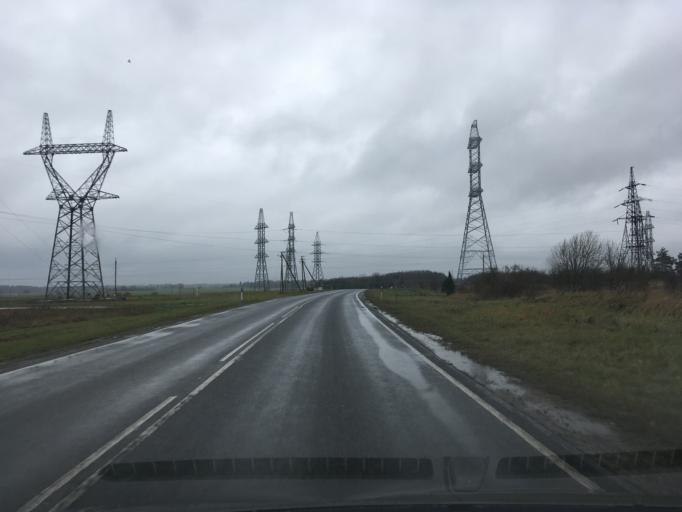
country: EE
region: Laeaene
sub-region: Lihula vald
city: Lihula
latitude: 58.6764
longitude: 23.8176
